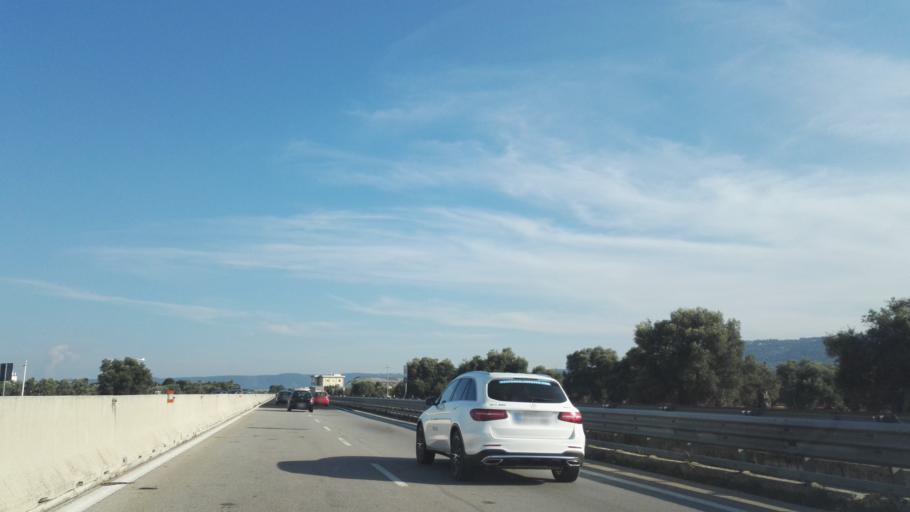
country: IT
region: Apulia
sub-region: Provincia di Brindisi
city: Fasano
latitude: 40.8637
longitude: 17.3469
